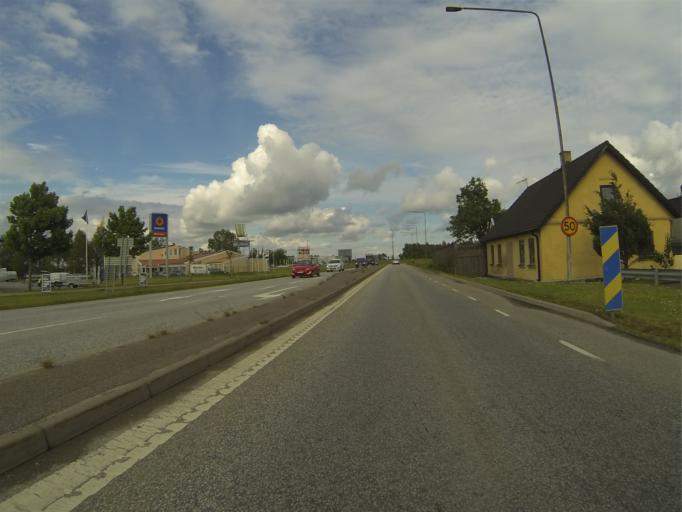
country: SE
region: Skane
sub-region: Staffanstorps Kommun
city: Staffanstorp
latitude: 55.6414
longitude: 13.2300
